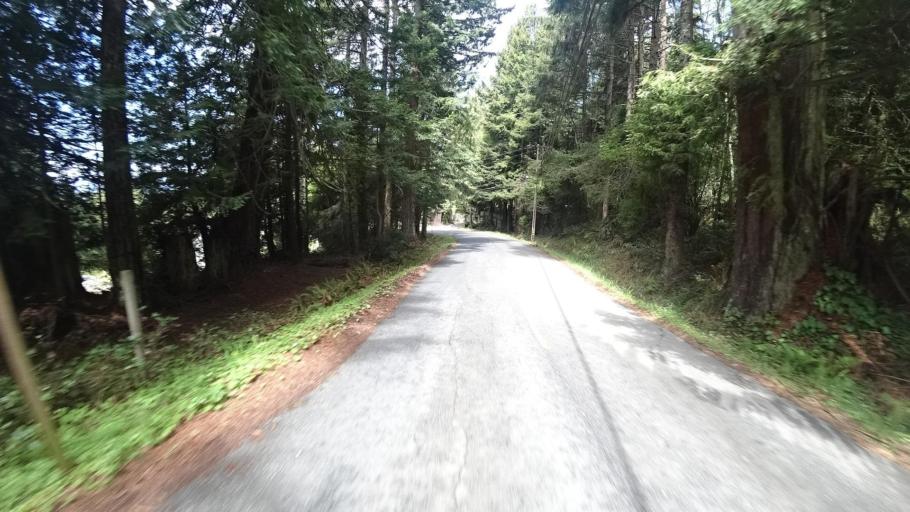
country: US
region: California
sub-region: Humboldt County
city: Bayside
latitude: 40.8658
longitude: -124.0469
